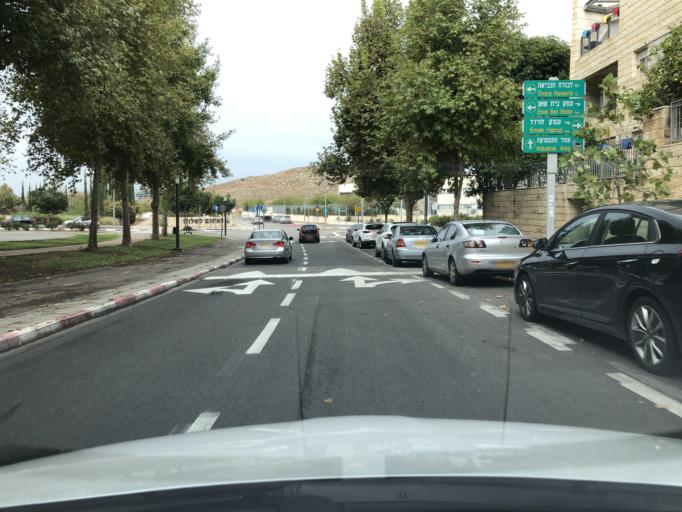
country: PS
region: West Bank
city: Al Midyah
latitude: 31.9175
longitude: 35.0035
